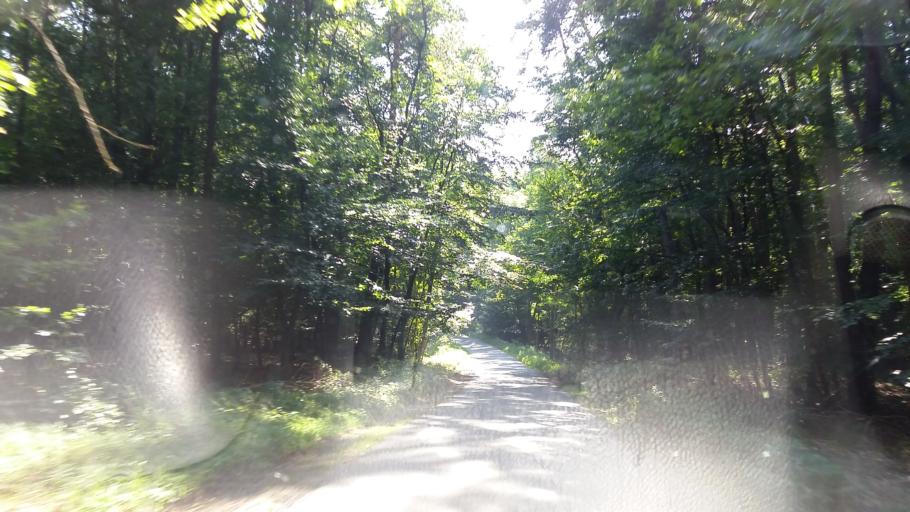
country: PL
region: West Pomeranian Voivodeship
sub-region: Powiat walecki
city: Czlopa
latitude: 53.0676
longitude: 15.9410
